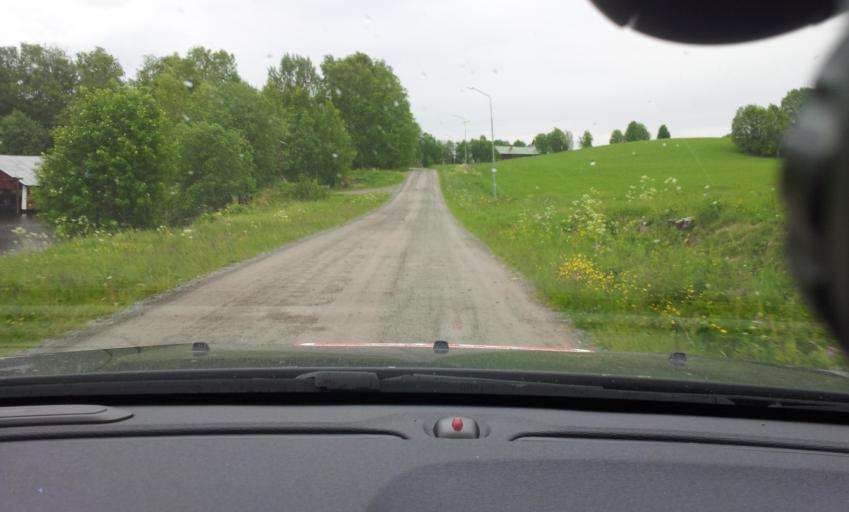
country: SE
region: Jaemtland
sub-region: OEstersunds Kommun
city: Ostersund
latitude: 62.9850
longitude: 14.5903
